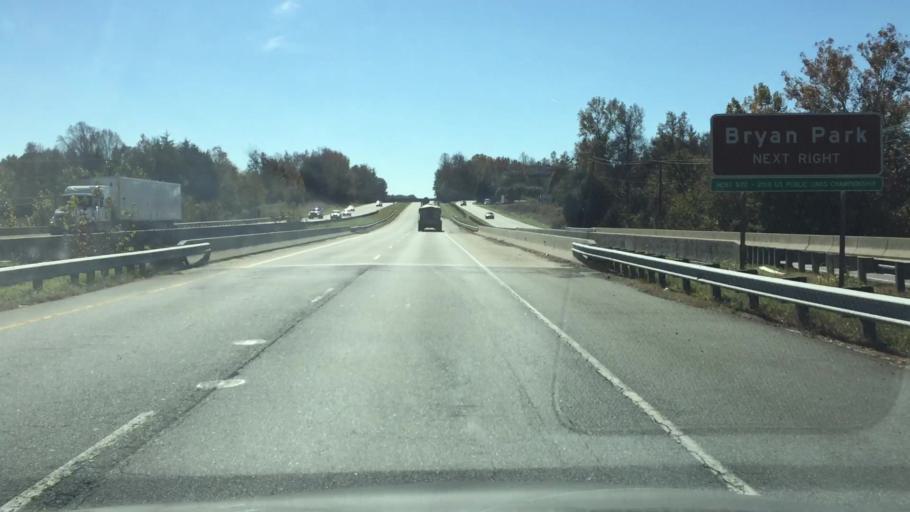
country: US
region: North Carolina
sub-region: Guilford County
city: McLeansville
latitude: 36.1819
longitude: -79.7083
